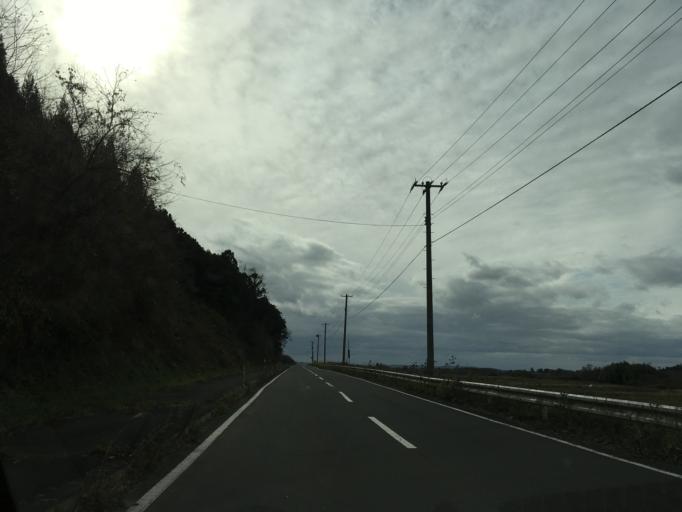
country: JP
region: Iwate
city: Ichinoseki
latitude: 38.7412
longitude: 141.2795
